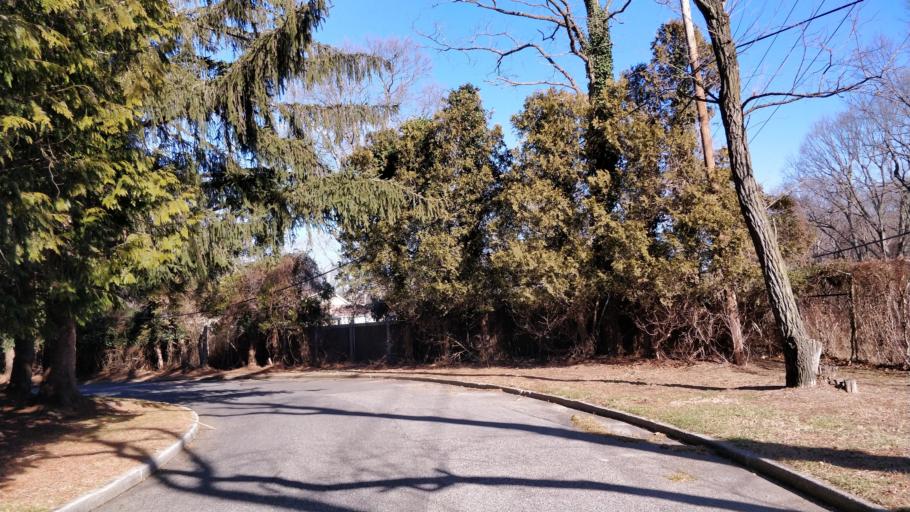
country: US
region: New York
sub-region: Suffolk County
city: Head of the Harbor
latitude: 40.9023
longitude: -73.1408
